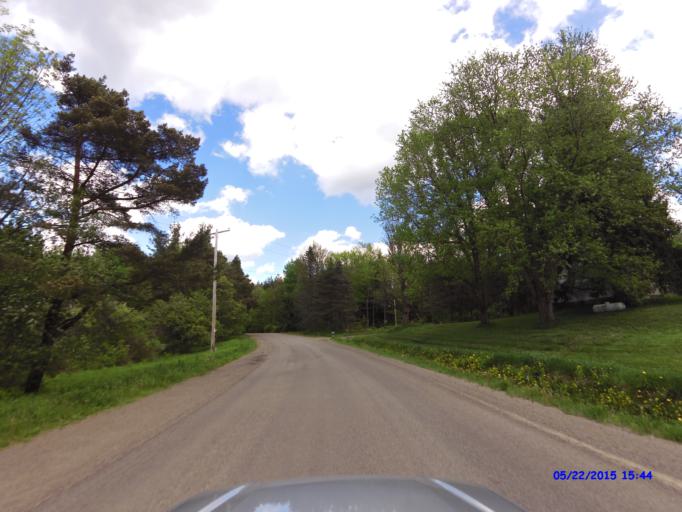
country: US
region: New York
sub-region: Cattaraugus County
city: Franklinville
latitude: 42.3124
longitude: -78.5481
